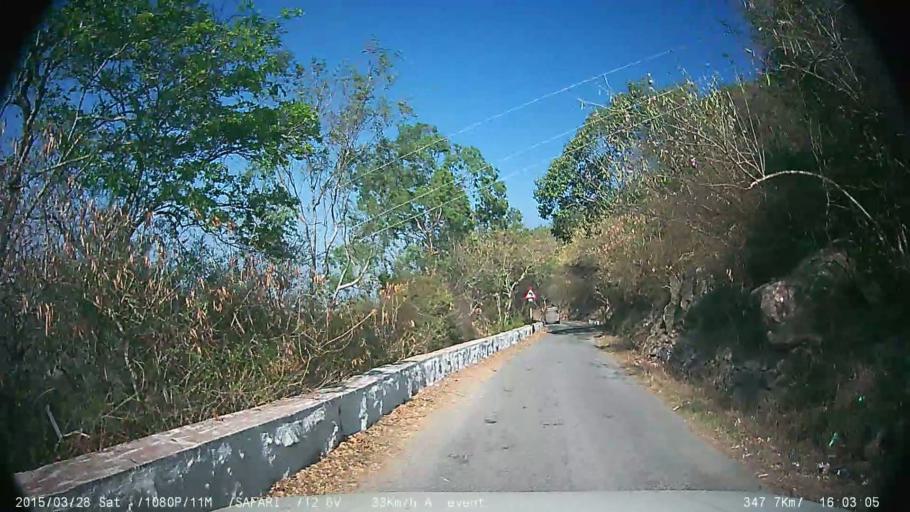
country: IN
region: Karnataka
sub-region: Mysore
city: Mysore
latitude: 12.2805
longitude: 76.6680
